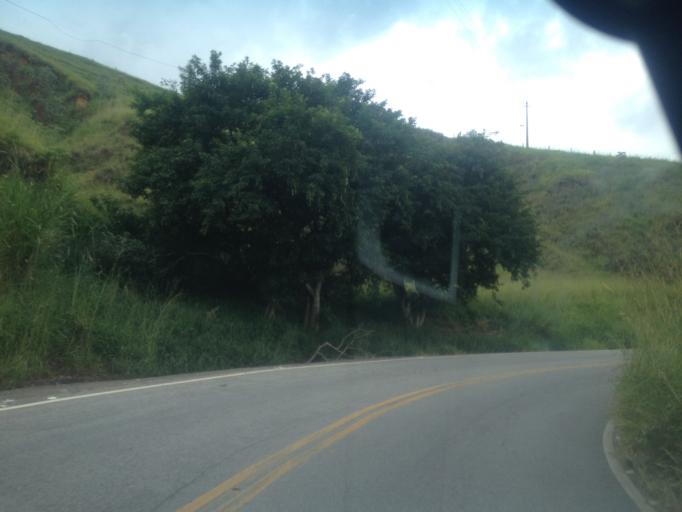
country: BR
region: Rio de Janeiro
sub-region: Quatis
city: Quatis
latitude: -22.3862
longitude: -44.2632
